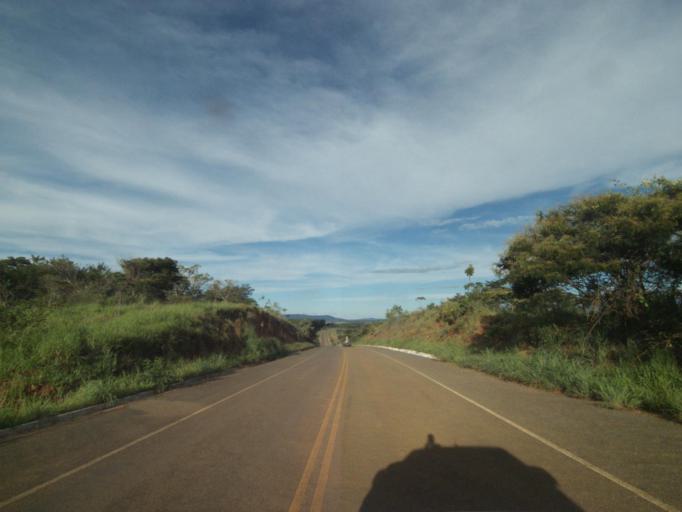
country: BR
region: Goias
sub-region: Jaragua
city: Jaragua
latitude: -15.8861
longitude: -49.4527
